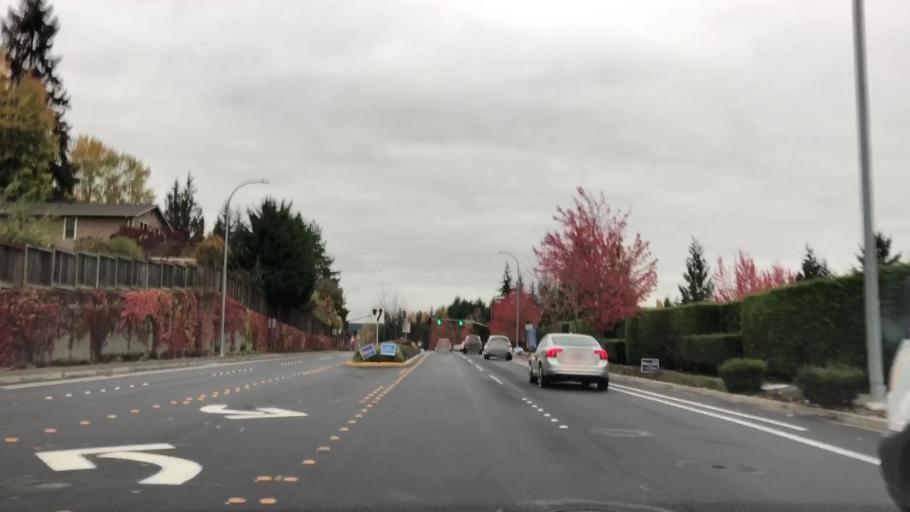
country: US
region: Washington
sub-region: King County
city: Newport
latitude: 47.5903
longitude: -122.1643
